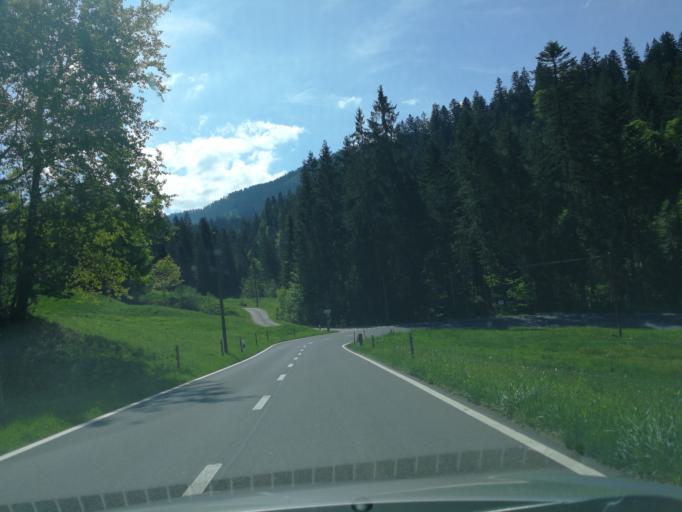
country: CH
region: Bern
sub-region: Emmental District
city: Eggiwil
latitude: 46.8204
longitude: 7.7849
